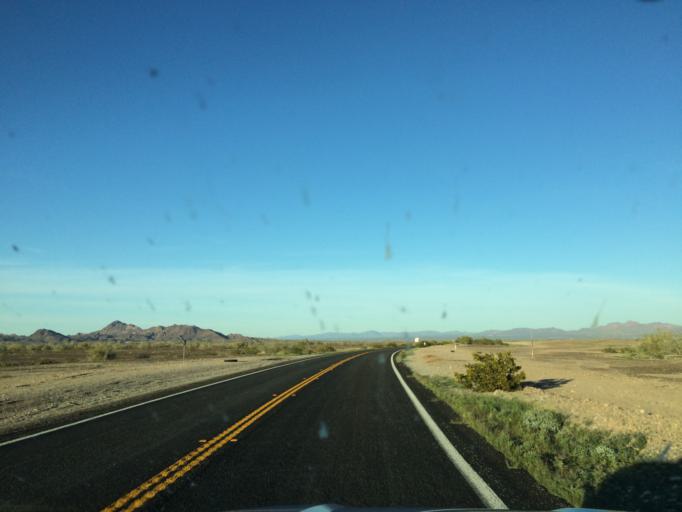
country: US
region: California
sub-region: Riverside County
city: Mesa Verde
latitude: 33.2434
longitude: -114.8298
